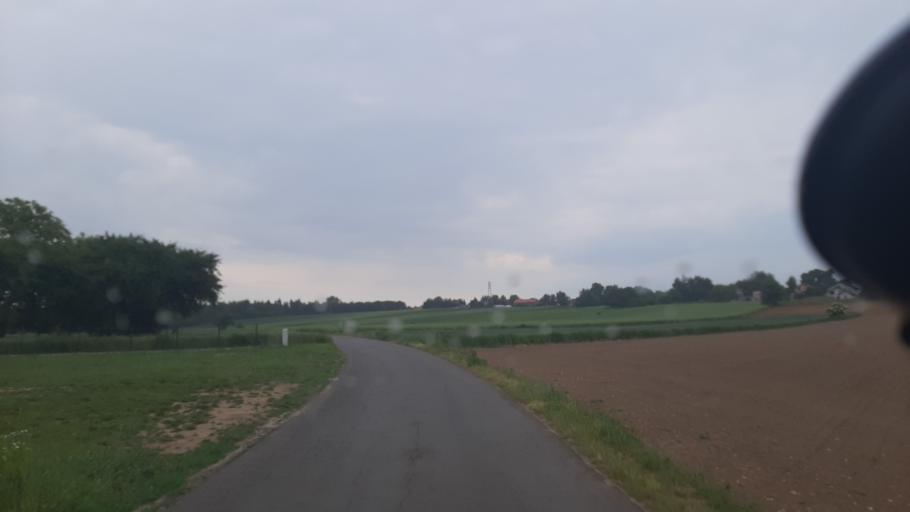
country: PL
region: Lublin Voivodeship
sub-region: Powiat lubelski
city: Garbow
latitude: 51.3520
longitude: 22.3582
